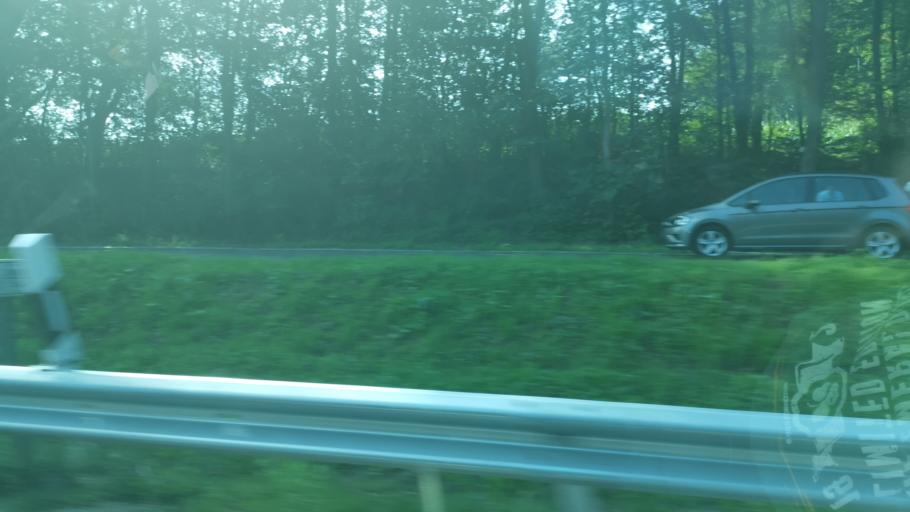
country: DE
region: Bavaria
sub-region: Upper Palatinate
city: Willmering
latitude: 49.2429
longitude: 12.6634
